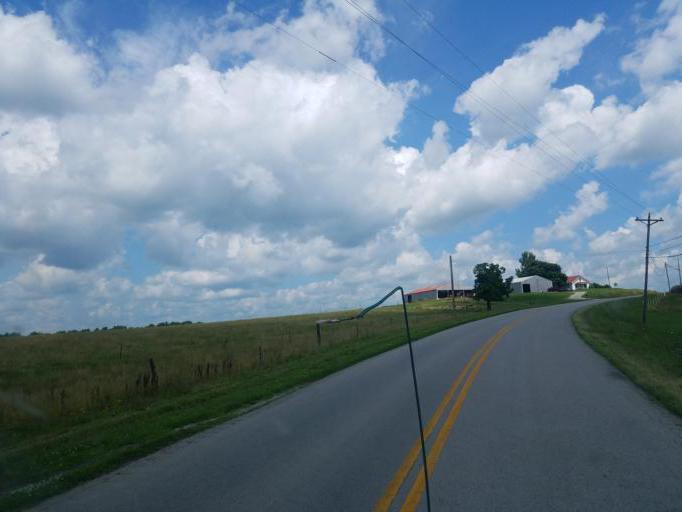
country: US
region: Kentucky
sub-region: Grayson County
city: Leitchfield
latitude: 37.5116
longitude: -86.3268
